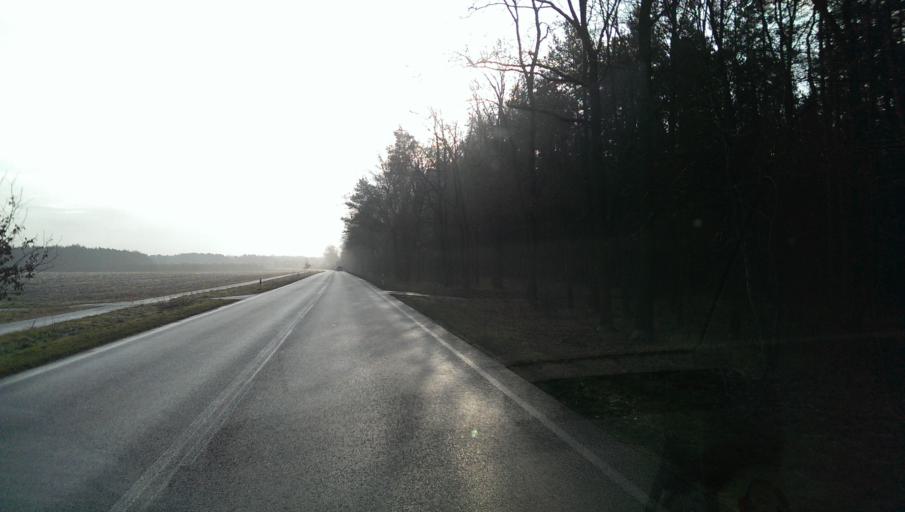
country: DE
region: Brandenburg
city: Bad Liebenwerda
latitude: 51.5371
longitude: 13.3966
